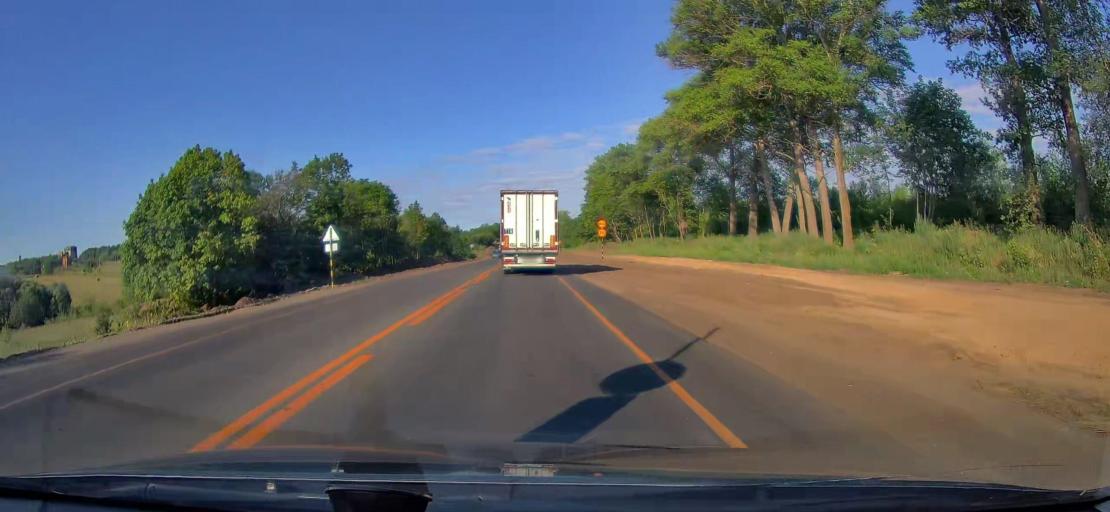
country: RU
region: Tula
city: Bol'shoye Skuratovo
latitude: 53.4499
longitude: 36.8527
